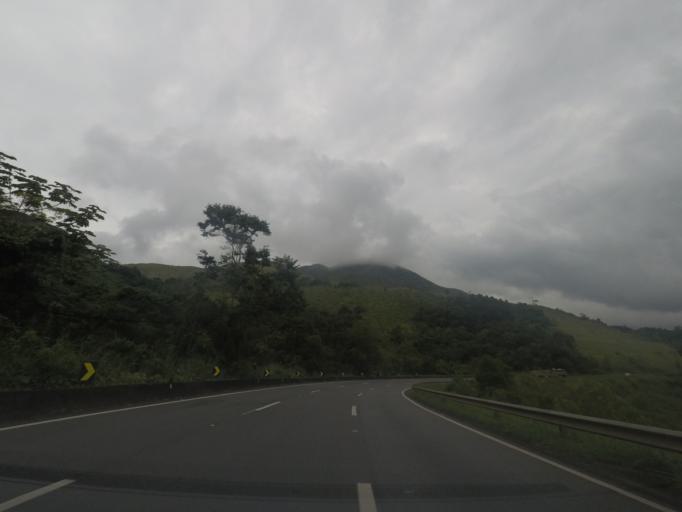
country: BR
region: Sao Paulo
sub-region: Cajati
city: Cajati
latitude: -24.9606
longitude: -48.4662
